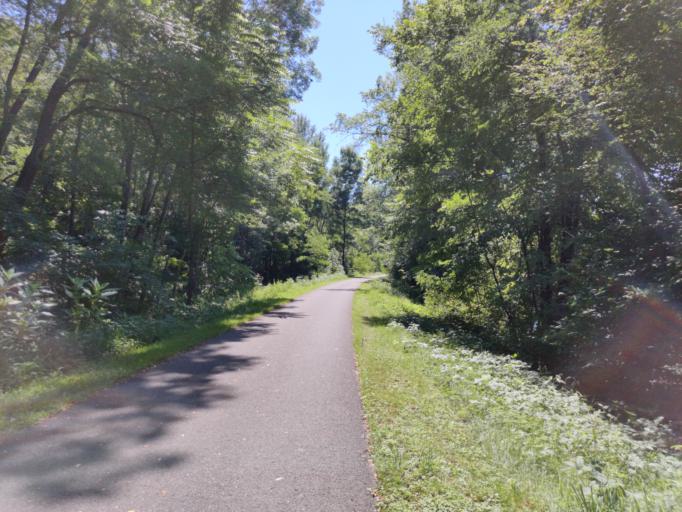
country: AT
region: Styria
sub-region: Politischer Bezirk Leibnitz
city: Obervogau
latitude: 46.7373
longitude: 15.5774
